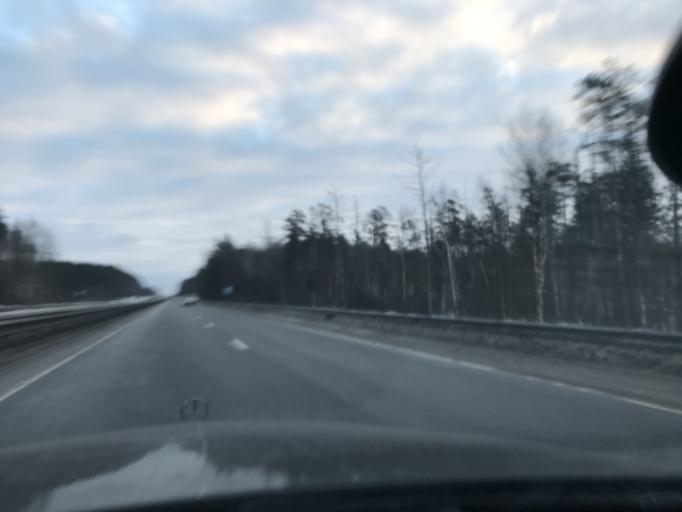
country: RU
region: Vladimir
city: Nikologory
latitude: 56.2351
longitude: 41.8780
